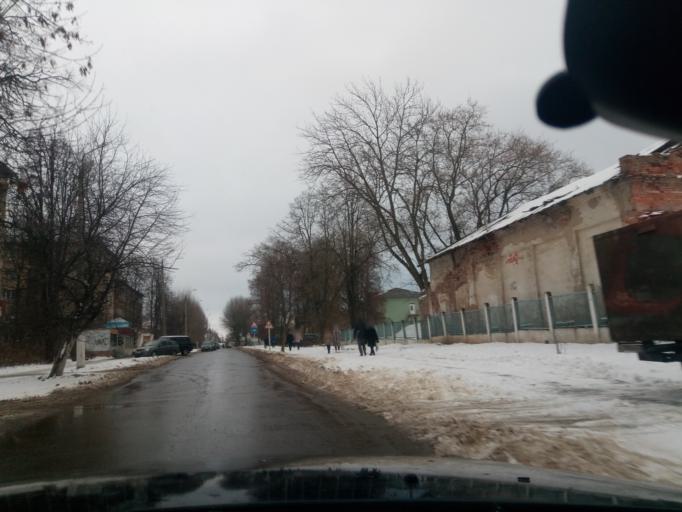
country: RU
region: Tula
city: Novomoskovsk
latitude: 54.0144
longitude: 38.2809
